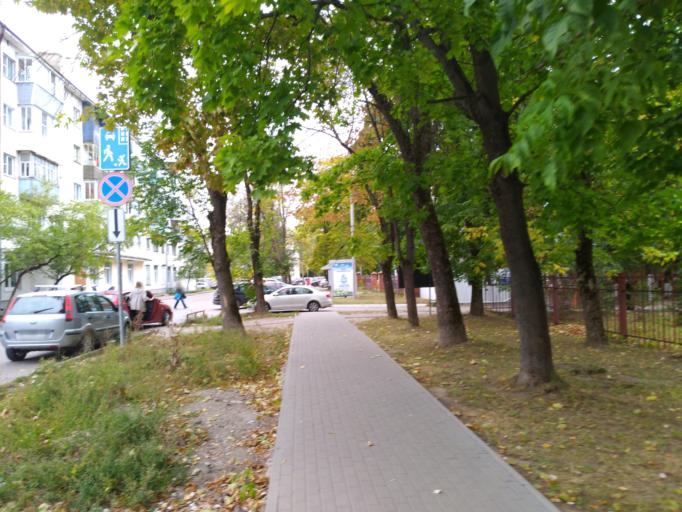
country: RU
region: Kaluga
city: Kaluga
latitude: 54.5348
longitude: 36.2586
